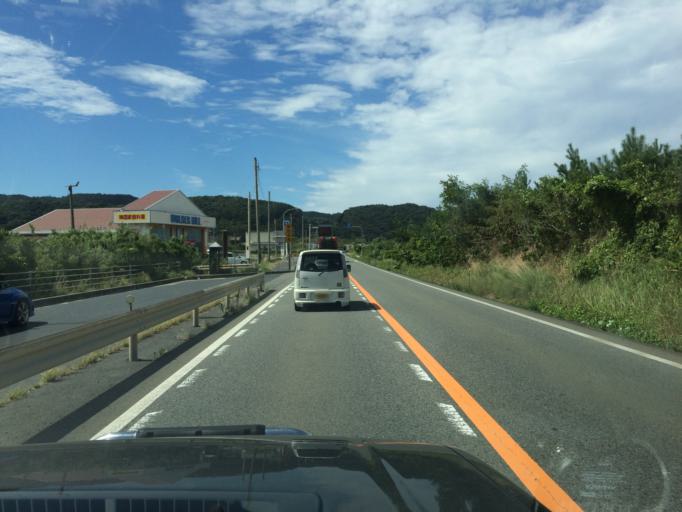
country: JP
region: Tottori
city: Tottori
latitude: 35.5177
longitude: 134.0362
